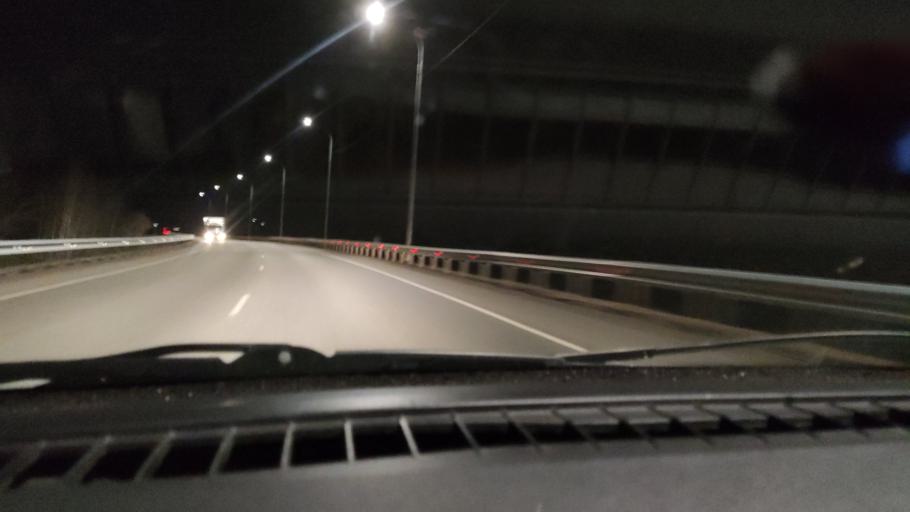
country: RU
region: Bashkortostan
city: Yermolayevo
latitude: 52.6531
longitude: 55.8366
